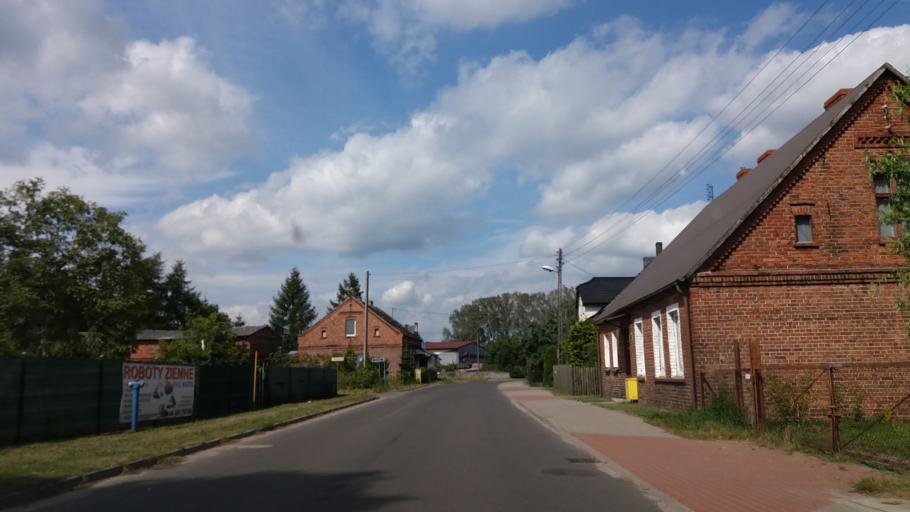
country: PL
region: West Pomeranian Voivodeship
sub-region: Powiat stargardzki
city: Kobylanka
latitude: 53.3488
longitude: 14.8685
